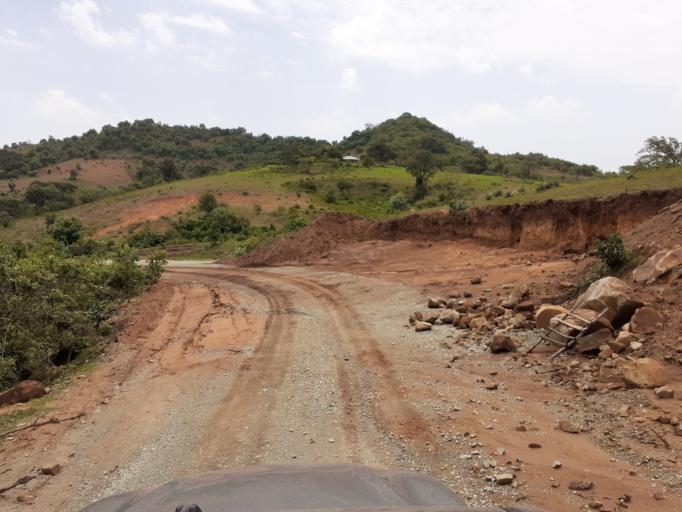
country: ET
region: Oromiya
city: Gimbi
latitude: 9.3347
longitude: 35.7003
